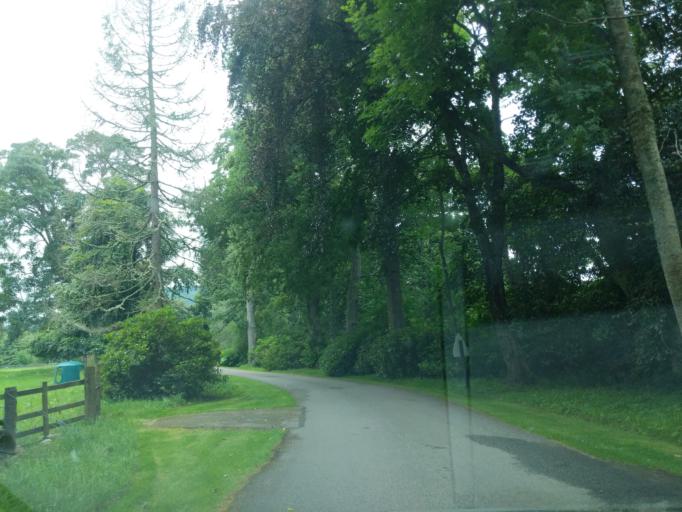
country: GB
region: Scotland
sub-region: Moray
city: Rothes
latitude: 57.4157
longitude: -3.3722
